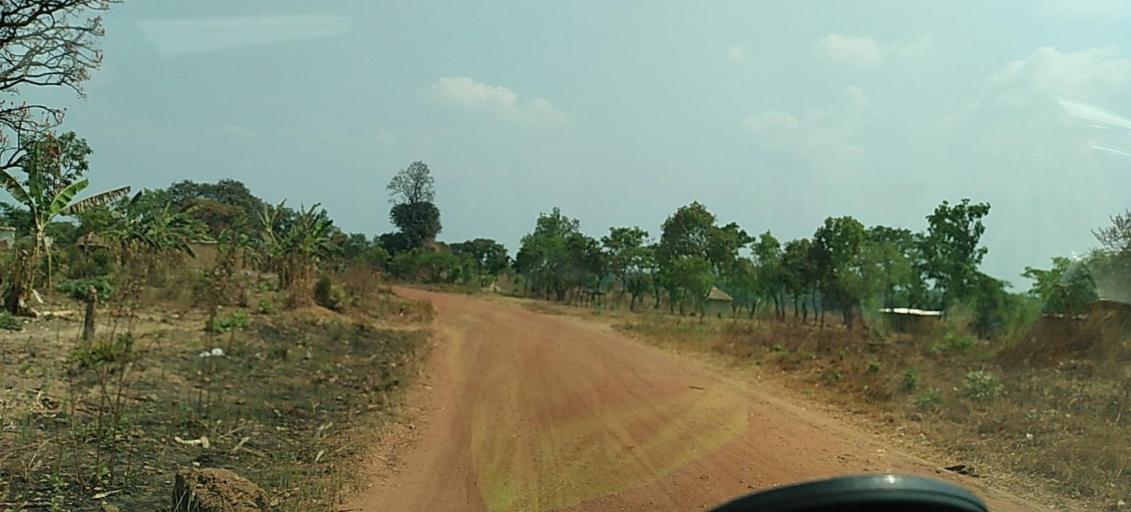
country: ZM
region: North-Western
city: Kansanshi
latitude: -12.0962
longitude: 26.3631
